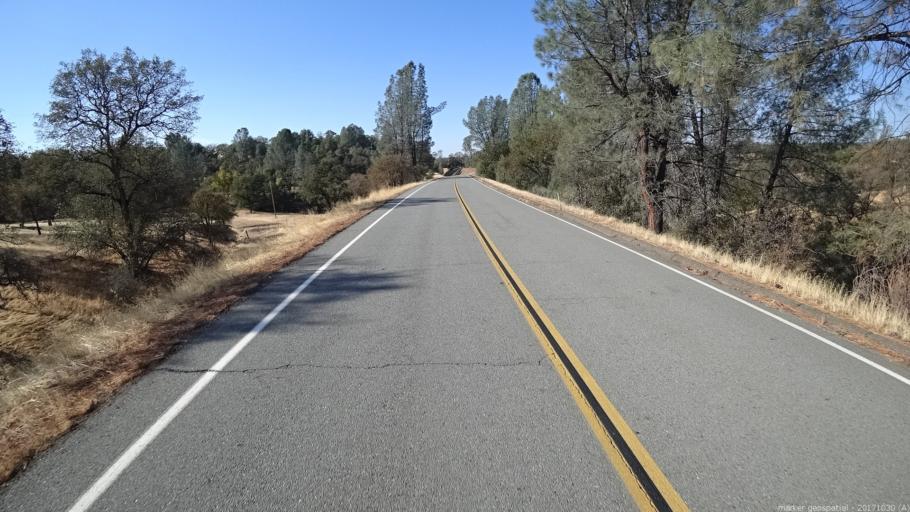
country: US
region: California
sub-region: Shasta County
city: Bella Vista
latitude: 40.6652
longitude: -122.0637
